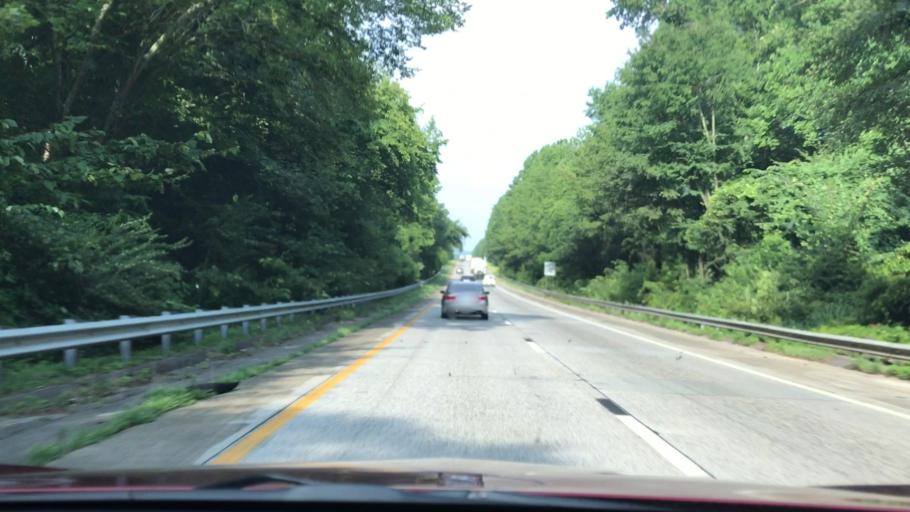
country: US
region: South Carolina
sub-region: Aiken County
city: Belvedere
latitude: 33.5448
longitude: -81.9739
